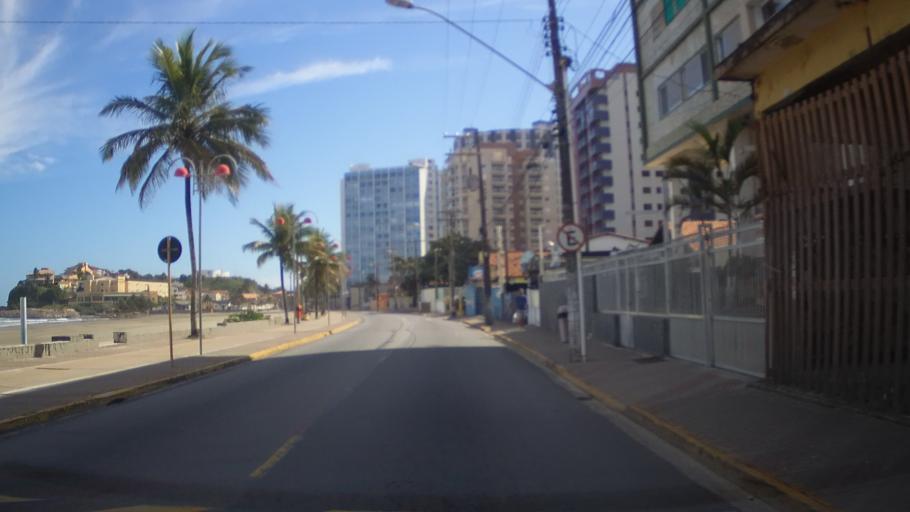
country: BR
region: Sao Paulo
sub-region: Itanhaem
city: Itanhaem
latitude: -24.1935
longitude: -46.7989
